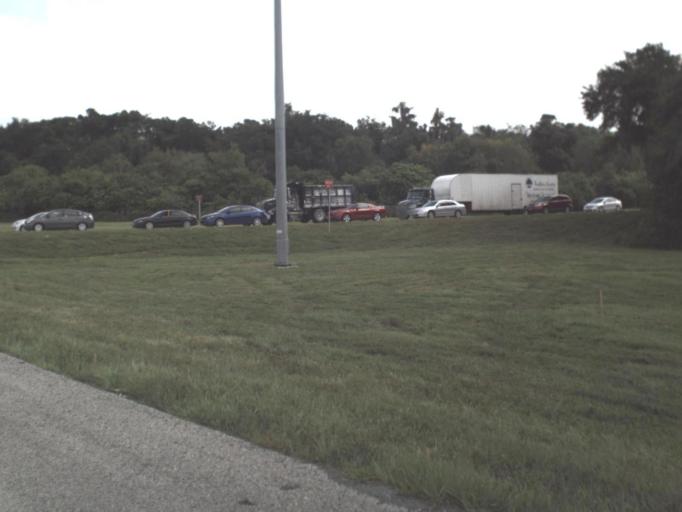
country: US
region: Florida
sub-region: Manatee County
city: Ellenton
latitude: 27.4909
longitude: -82.4712
